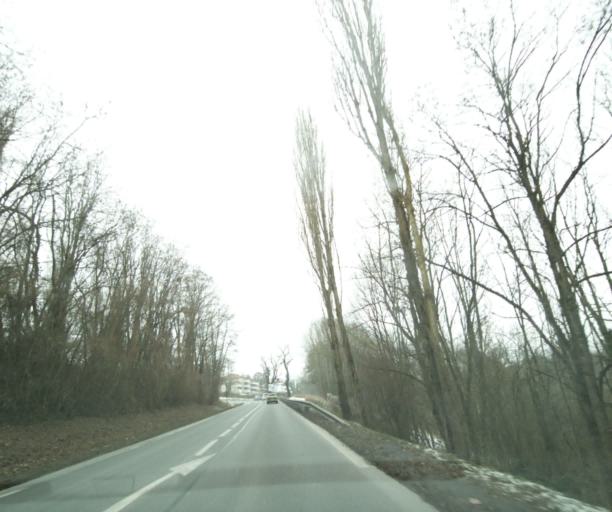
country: FR
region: Rhone-Alpes
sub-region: Departement de la Haute-Savoie
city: Reignier-Esery
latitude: 46.1405
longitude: 6.2689
